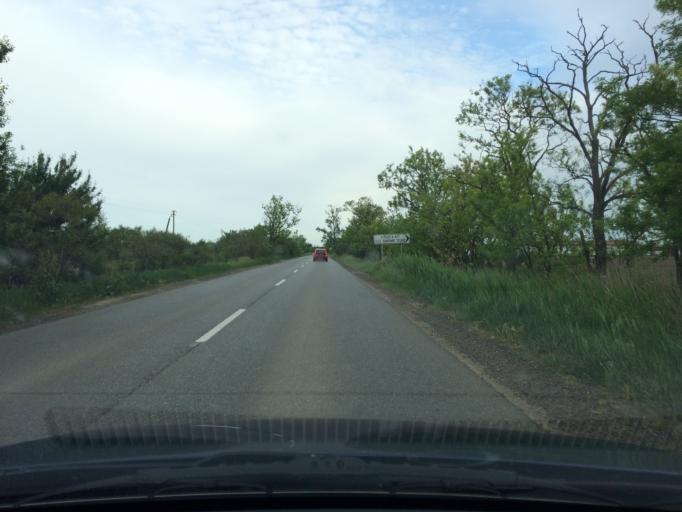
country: HU
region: Szabolcs-Szatmar-Bereg
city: Tiszavasvari
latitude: 47.9256
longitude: 21.3888
